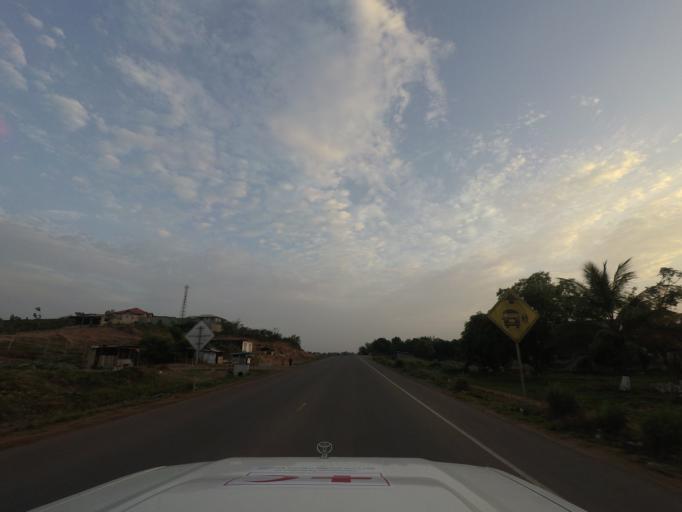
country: LR
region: Montserrado
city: Bensonville City
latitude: 6.3335
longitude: -10.6584
